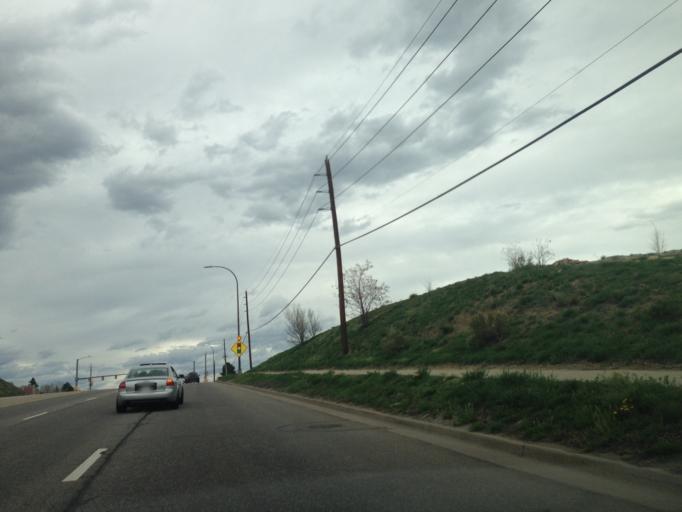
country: US
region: Colorado
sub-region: Jefferson County
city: Arvada
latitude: 39.8250
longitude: -105.0813
